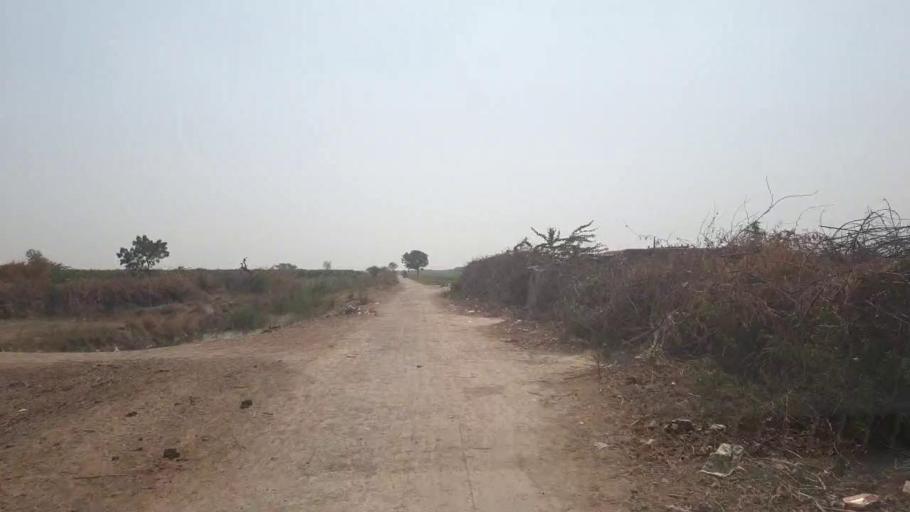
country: PK
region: Sindh
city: Dhoro Naro
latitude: 25.4870
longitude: 69.5648
